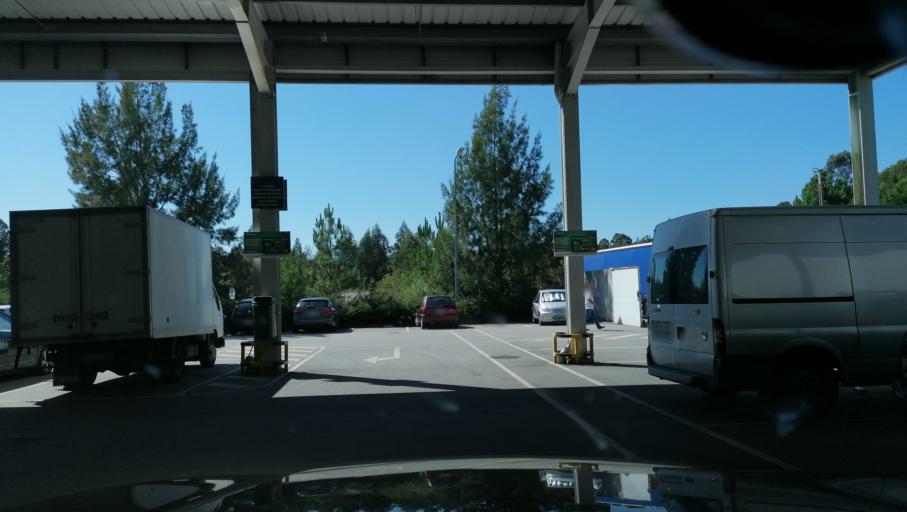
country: PT
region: Aveiro
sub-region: Santa Maria da Feira
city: Feira
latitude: 40.9325
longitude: -8.5274
